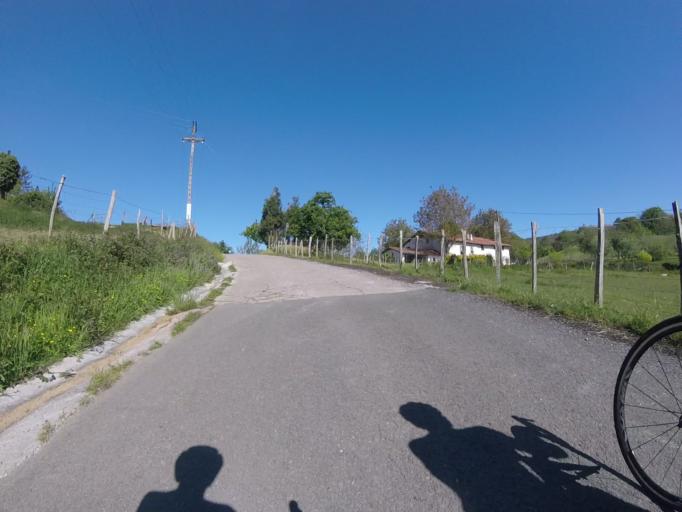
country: ES
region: Basque Country
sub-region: Provincia de Guipuzcoa
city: Errezil
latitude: 43.1712
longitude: -2.2043
